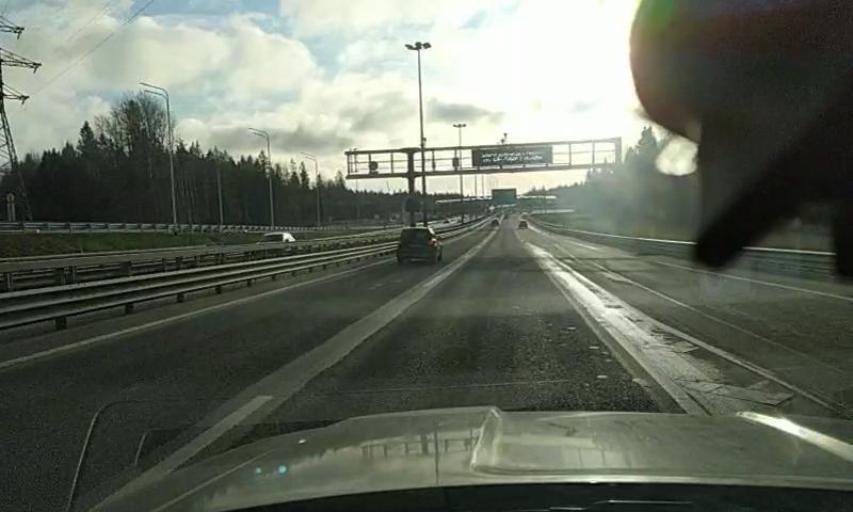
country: RU
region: St.-Petersburg
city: Beloostrov
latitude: 60.1326
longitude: 30.0611
